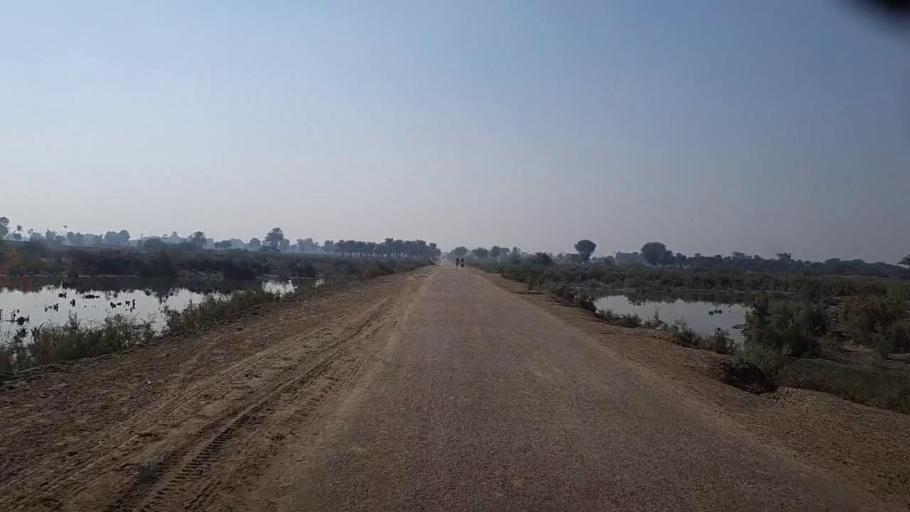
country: PK
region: Sindh
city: Bozdar
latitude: 27.2506
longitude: 68.6102
